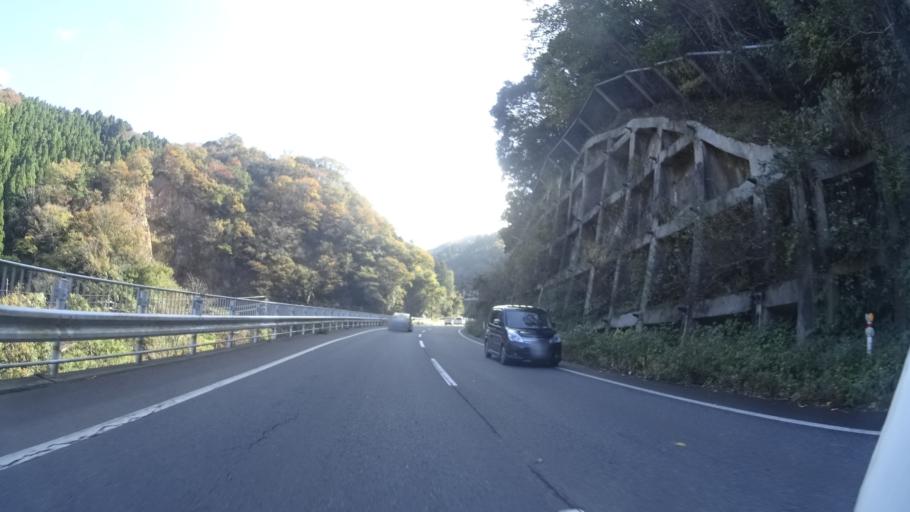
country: JP
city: Asahi
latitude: 35.9592
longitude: 135.9968
